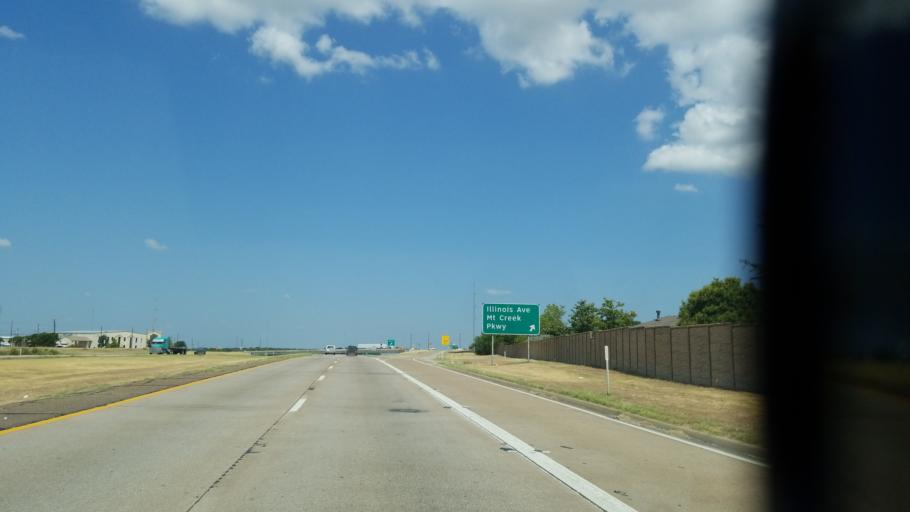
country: US
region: Texas
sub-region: Dallas County
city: Cockrell Hill
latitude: 32.7169
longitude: -96.9130
